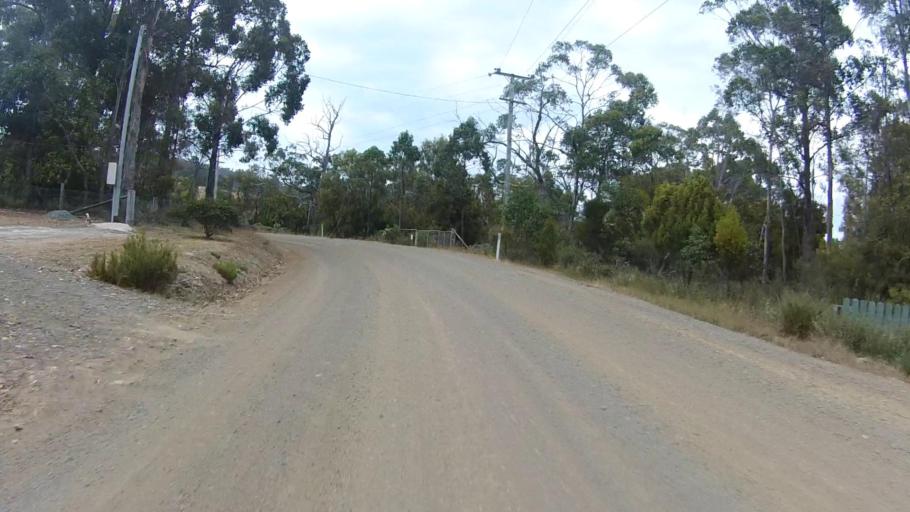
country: AU
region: Tasmania
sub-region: Huon Valley
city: Cygnet
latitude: -43.2303
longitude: 147.0973
